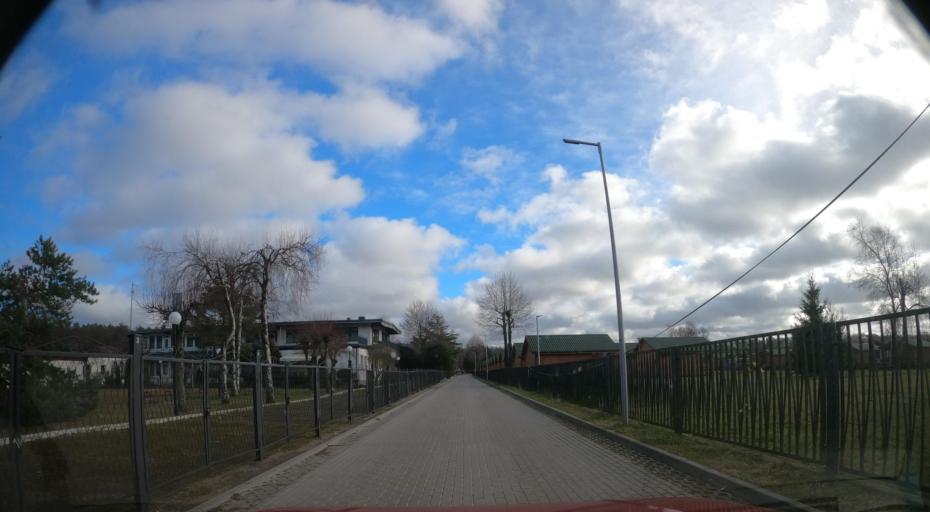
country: PL
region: West Pomeranian Voivodeship
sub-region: Powiat koszalinski
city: Sianow
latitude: 54.3141
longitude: 16.2059
